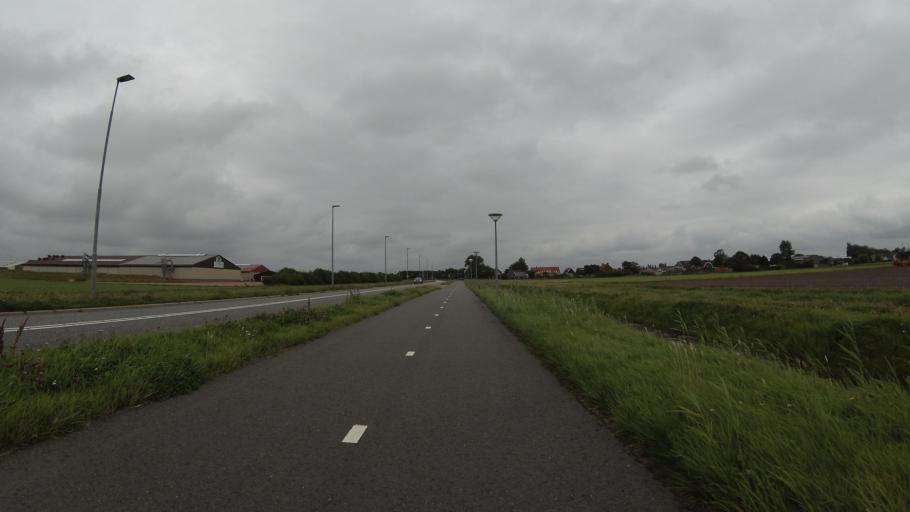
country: NL
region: North Holland
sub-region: Gemeente Den Helder
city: Den Helder
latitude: 52.9013
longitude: 4.7483
